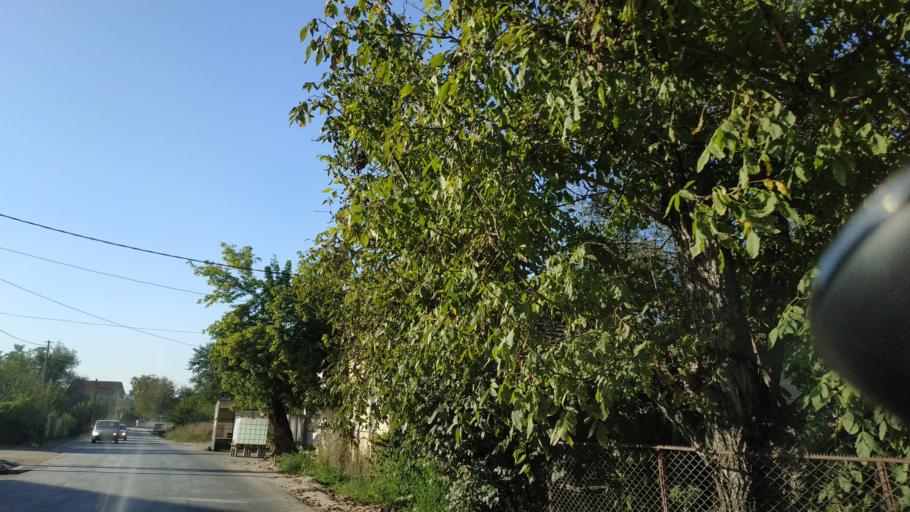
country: RS
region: Central Serbia
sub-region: Rasinski Okrug
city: Krusevac
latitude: 43.4997
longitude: 21.3412
